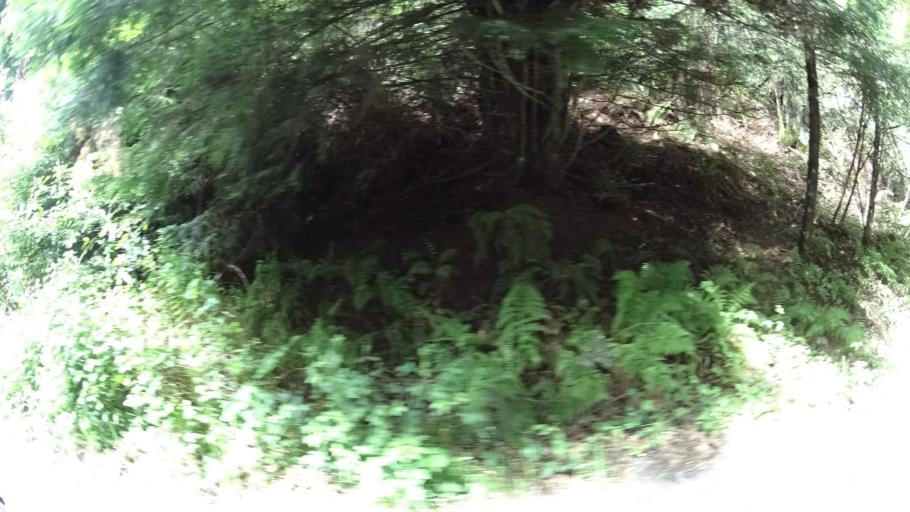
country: US
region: California
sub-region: Humboldt County
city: Blue Lake
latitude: 40.9083
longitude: -124.0373
